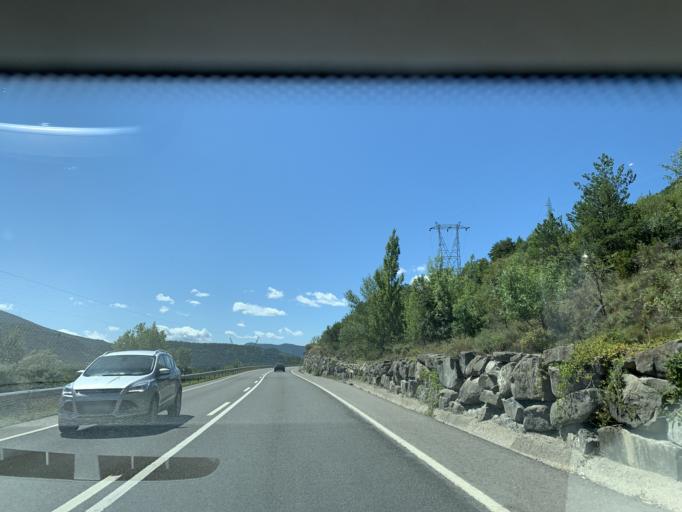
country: ES
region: Aragon
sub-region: Provincia de Huesca
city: Biescas
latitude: 42.5720
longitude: -0.3251
